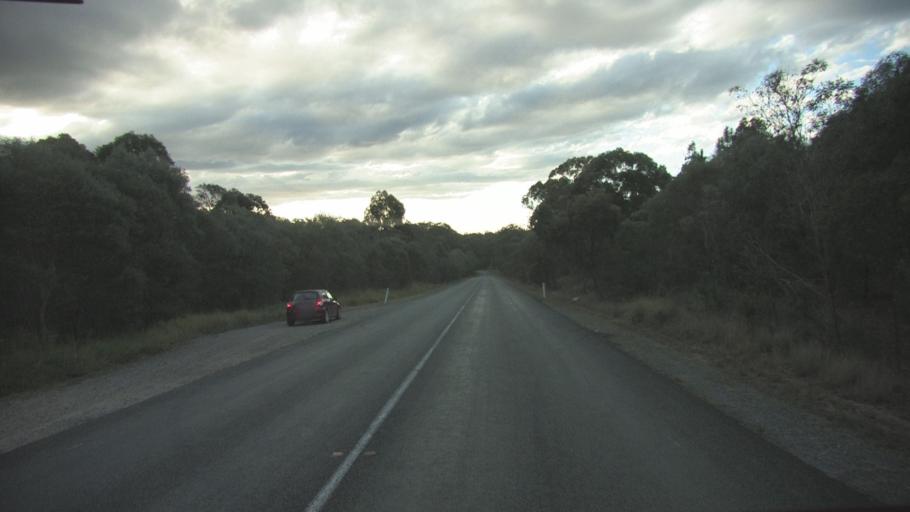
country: AU
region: Queensland
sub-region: Logan
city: Chambers Flat
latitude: -27.7973
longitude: 153.1417
